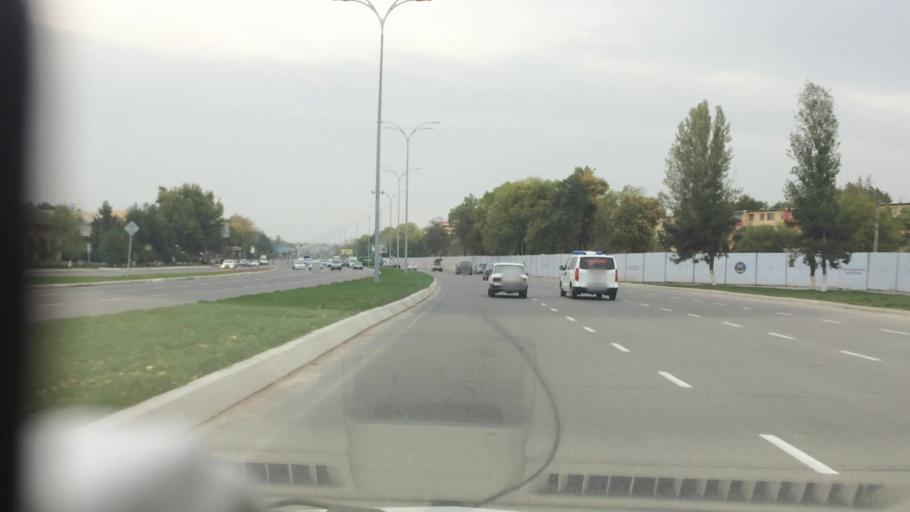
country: UZ
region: Toshkent
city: Salor
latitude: 41.3015
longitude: 69.3446
